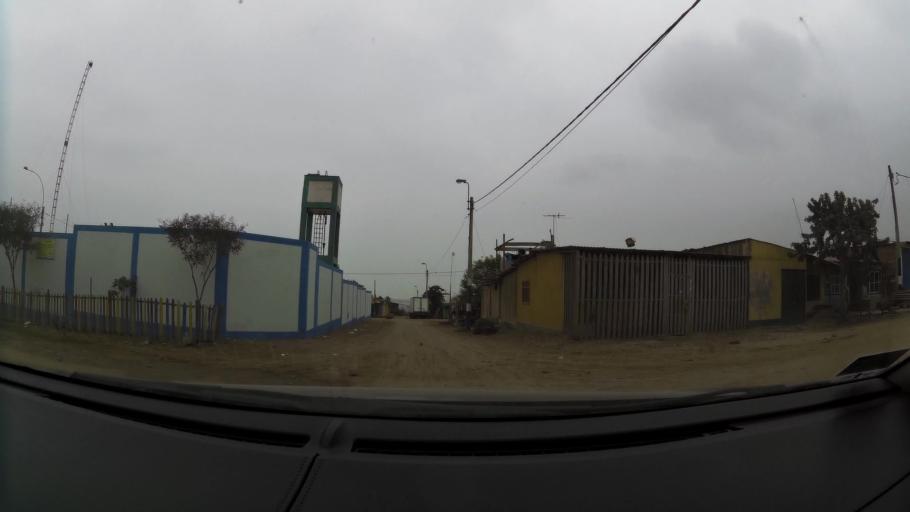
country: PE
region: Lima
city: Ventanilla
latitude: -11.8454
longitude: -77.1425
